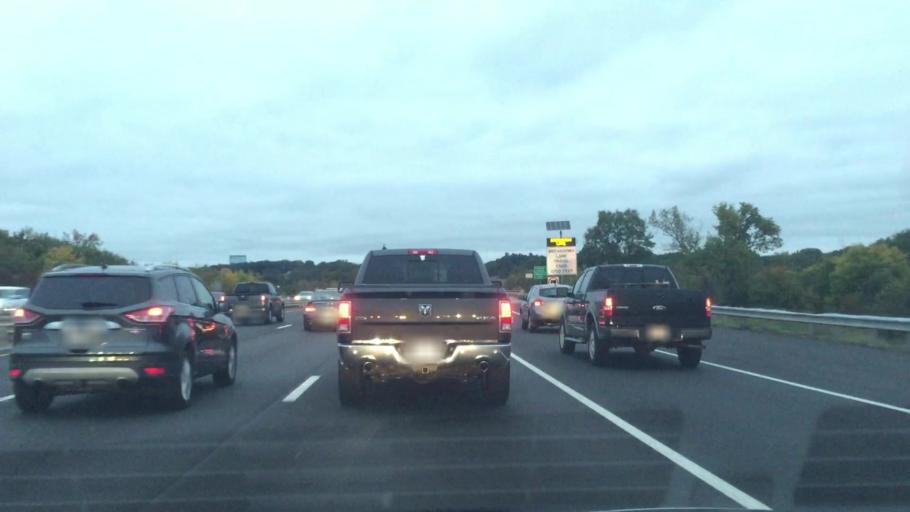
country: US
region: Massachusetts
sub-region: Essex County
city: Methuen
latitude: 42.6980
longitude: -71.2093
